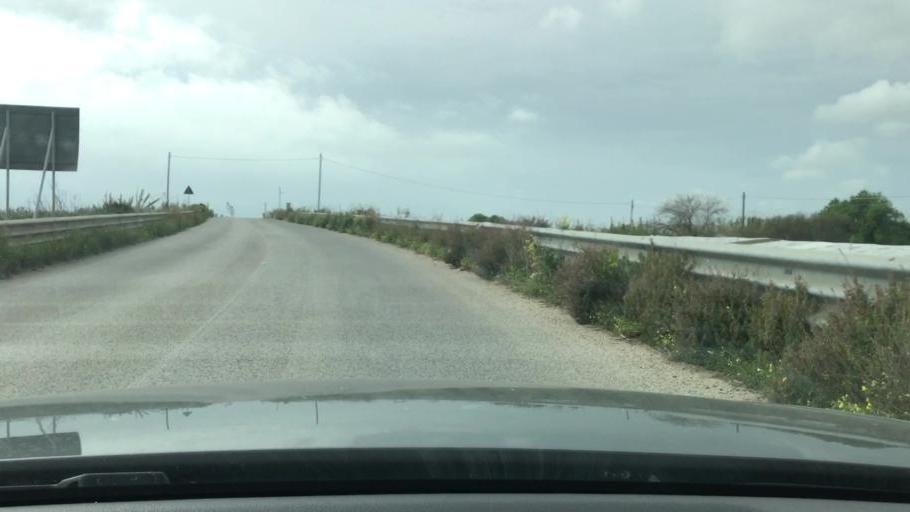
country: IT
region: Sicily
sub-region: Ragusa
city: Cava d'Aliga
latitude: 36.7514
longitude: 14.6708
